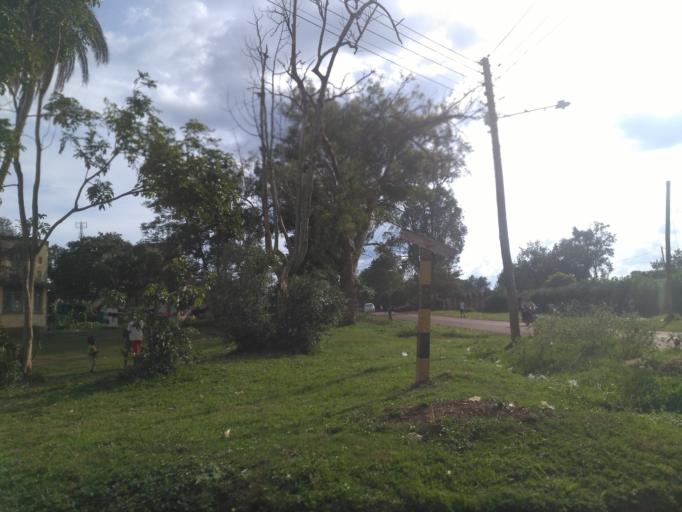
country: UG
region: Eastern Region
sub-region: Jinja District
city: Jinja
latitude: 0.4239
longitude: 33.2033
